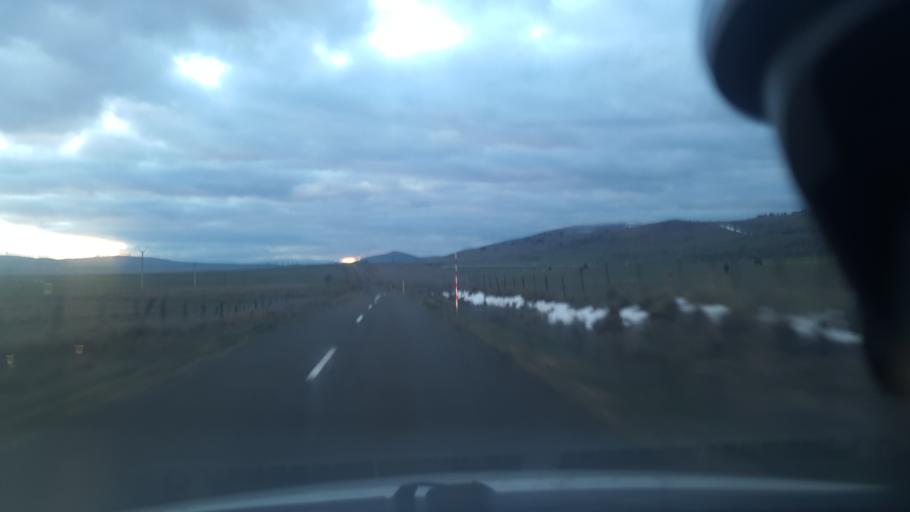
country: ES
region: Castille and Leon
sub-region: Provincia de Segovia
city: Villacastin
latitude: 40.7027
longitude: -4.3686
